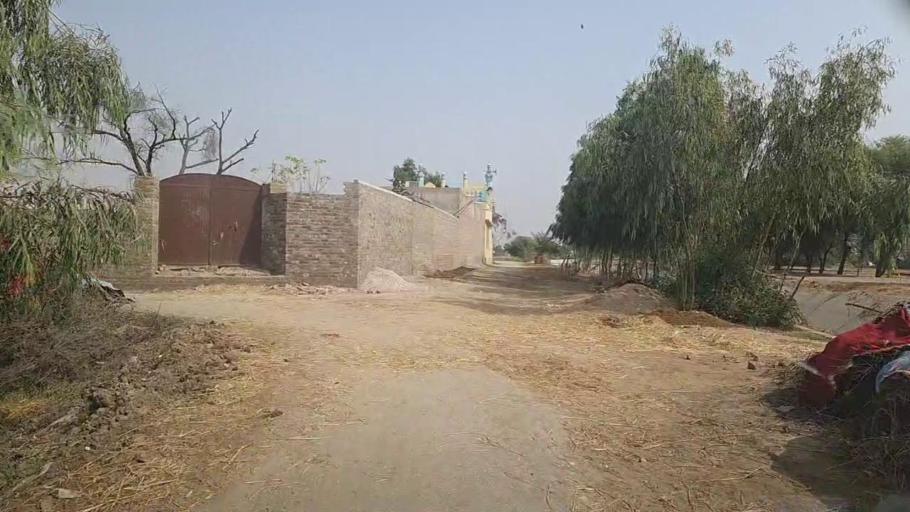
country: PK
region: Sindh
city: Kashmor
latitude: 28.4579
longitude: 69.5503
